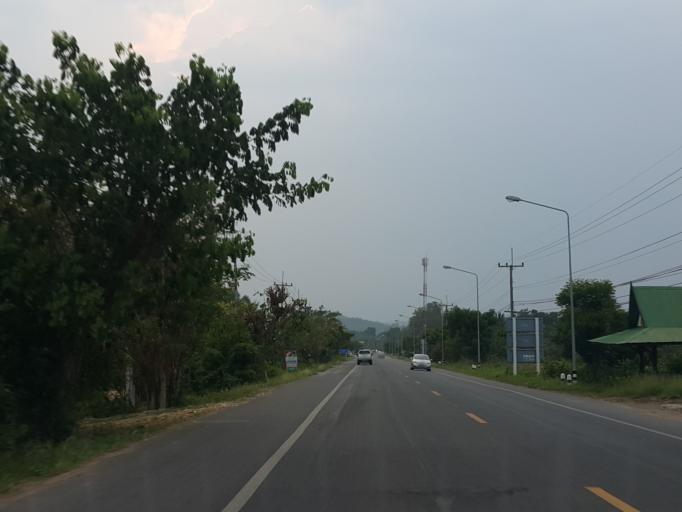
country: TH
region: Uthai Thani
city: Ban Rai
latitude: 15.0869
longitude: 99.5836
